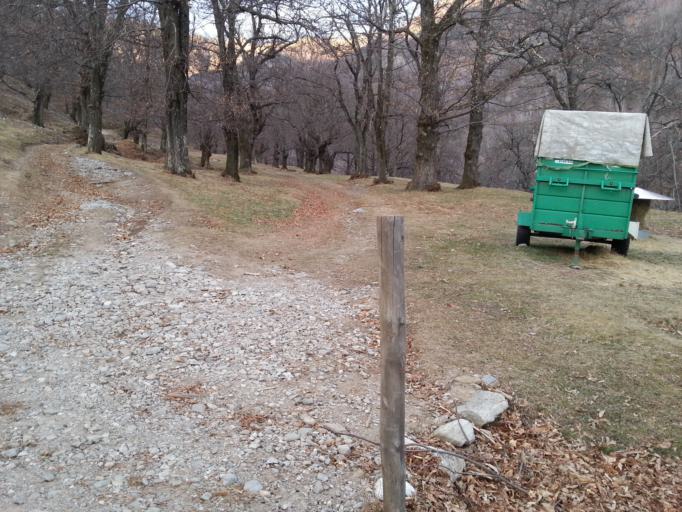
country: CH
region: Ticino
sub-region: Lugano District
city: Gravesano
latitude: 46.0507
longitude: 8.8833
